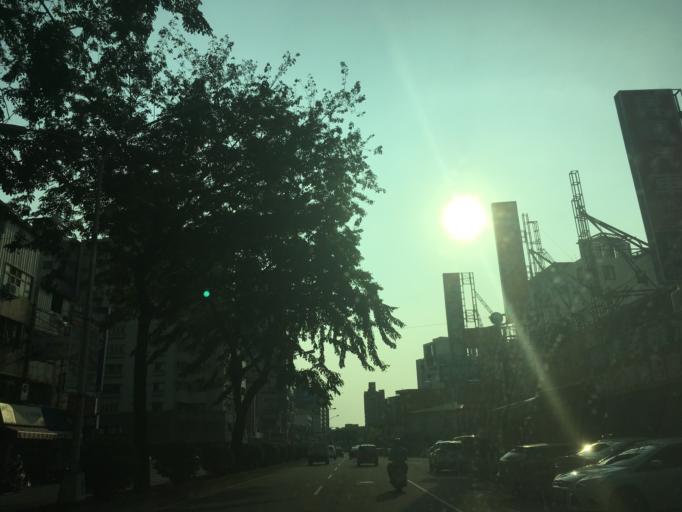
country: TW
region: Taiwan
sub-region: Taichung City
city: Taichung
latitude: 24.1265
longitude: 120.6771
